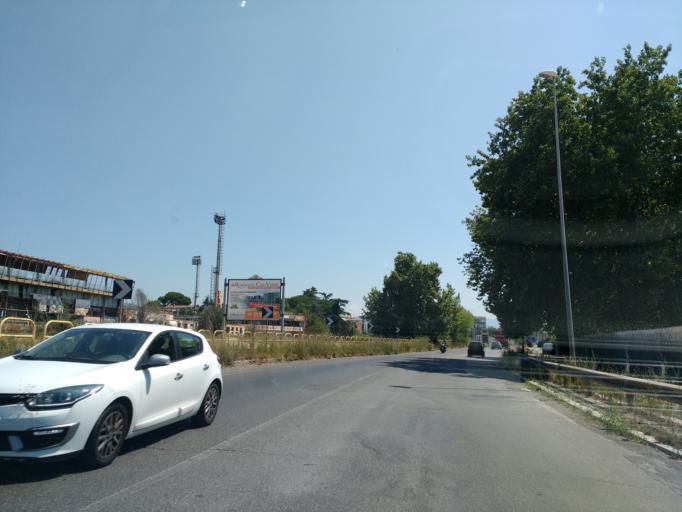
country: IT
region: Latium
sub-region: Citta metropolitana di Roma Capitale
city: Albuccione
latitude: 41.9518
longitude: 12.6879
